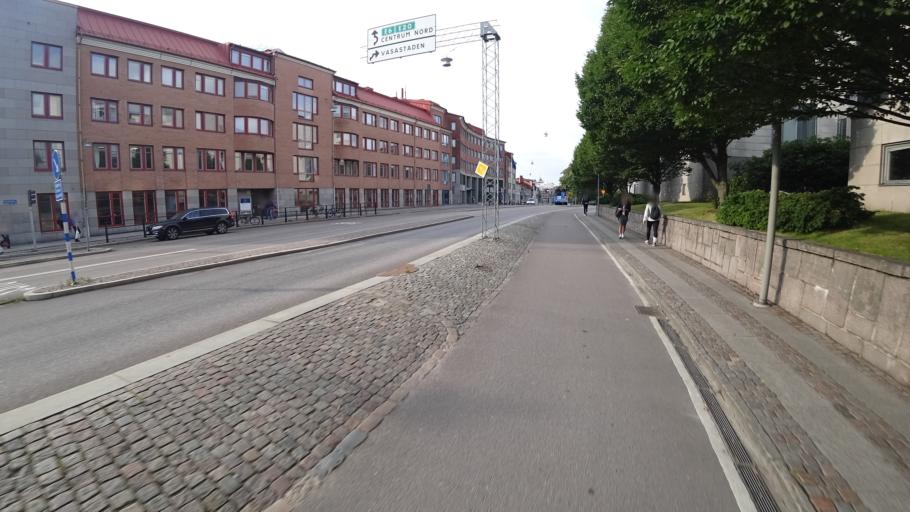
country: SE
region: Vaestra Goetaland
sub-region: Goteborg
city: Goeteborg
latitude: 57.6969
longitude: 11.9607
